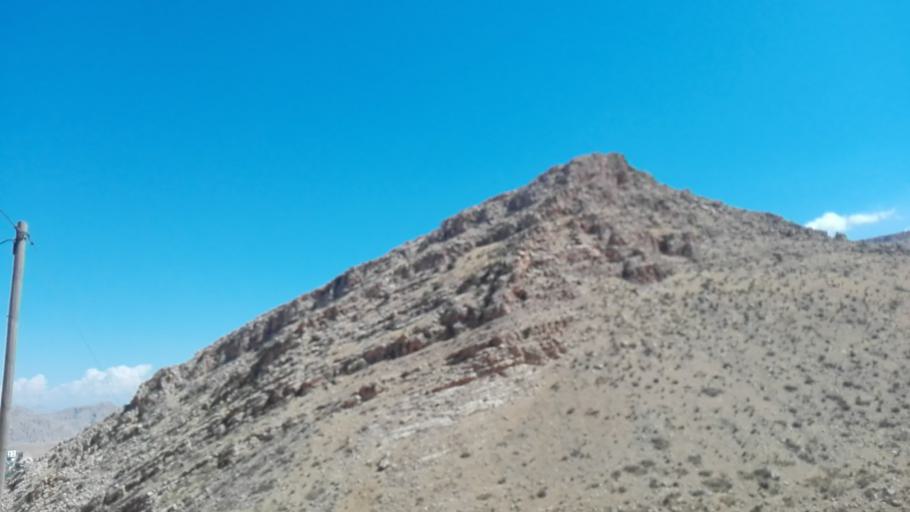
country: TR
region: Batman
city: Hasankeyf
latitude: 37.6984
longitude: 41.4583
